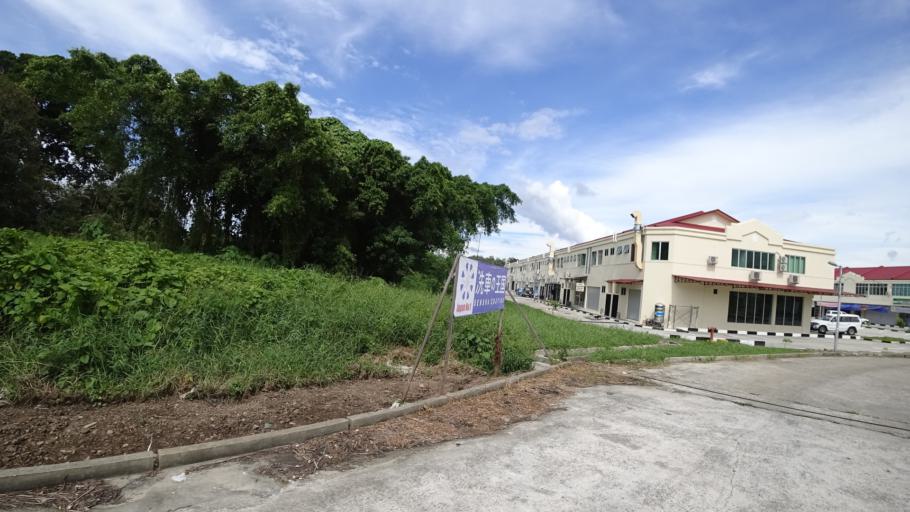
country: BN
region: Brunei and Muara
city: Bandar Seri Begawan
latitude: 4.8895
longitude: 114.8412
